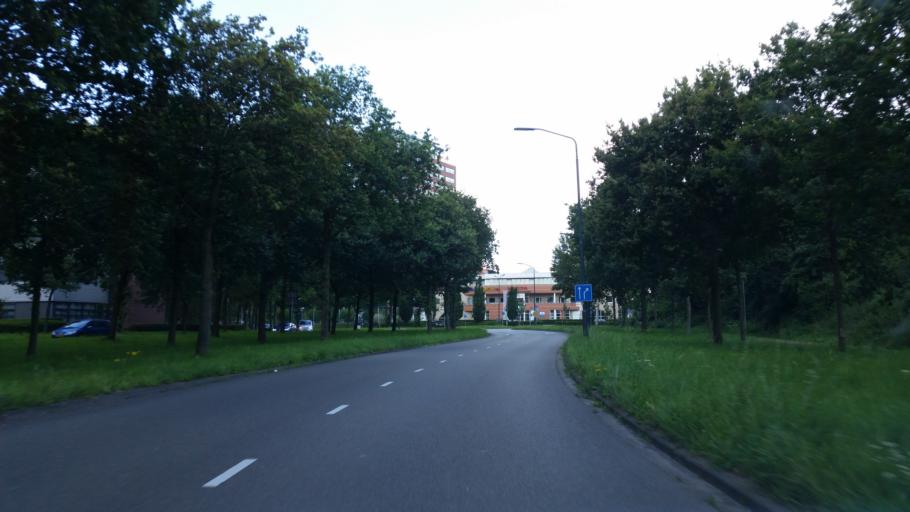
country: NL
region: North Brabant
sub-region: Gemeente Breda
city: Breda
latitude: 51.6052
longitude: 4.7245
